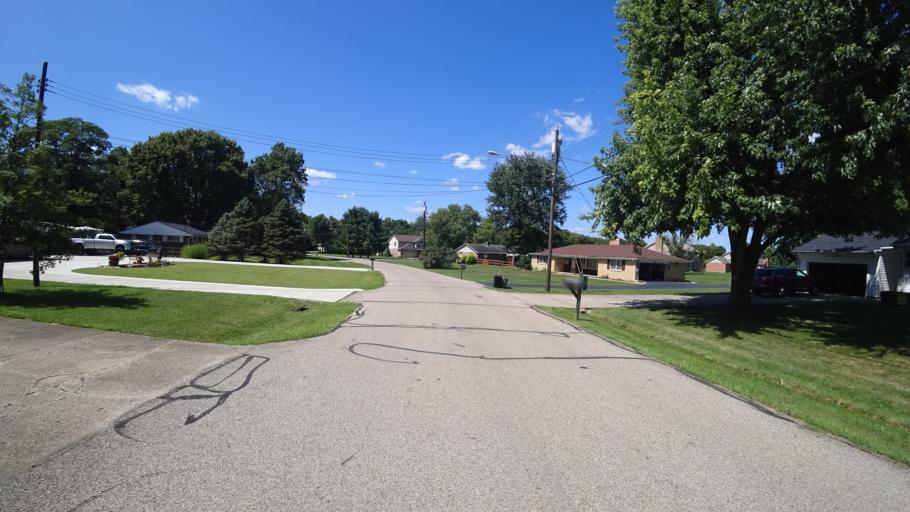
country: US
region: Ohio
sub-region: Butler County
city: New Miami
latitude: 39.4127
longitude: -84.5255
